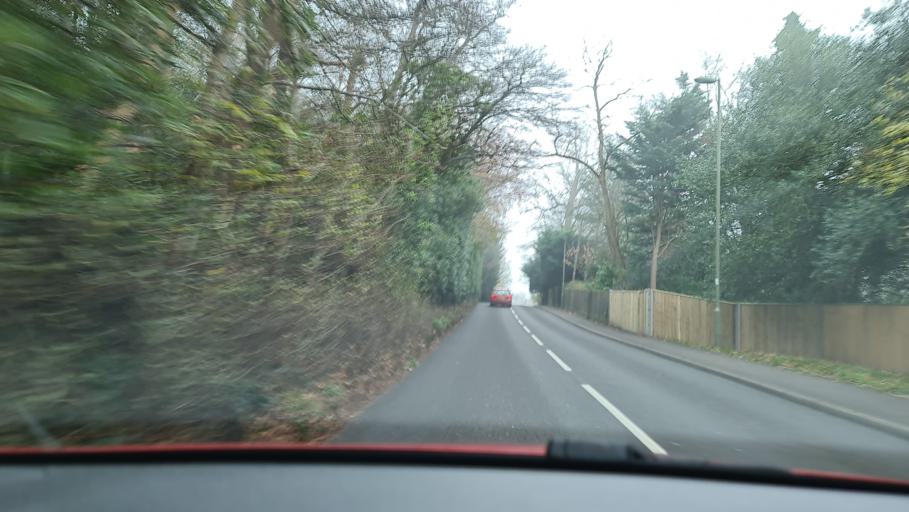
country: GB
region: England
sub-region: Surrey
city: Esher
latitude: 51.3348
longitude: -0.3594
